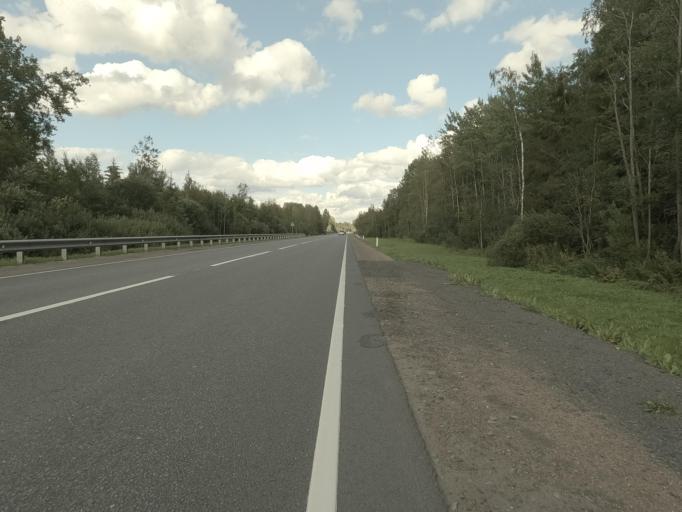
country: RU
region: Leningrad
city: Nikol'skoye
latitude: 59.6593
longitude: 30.8694
